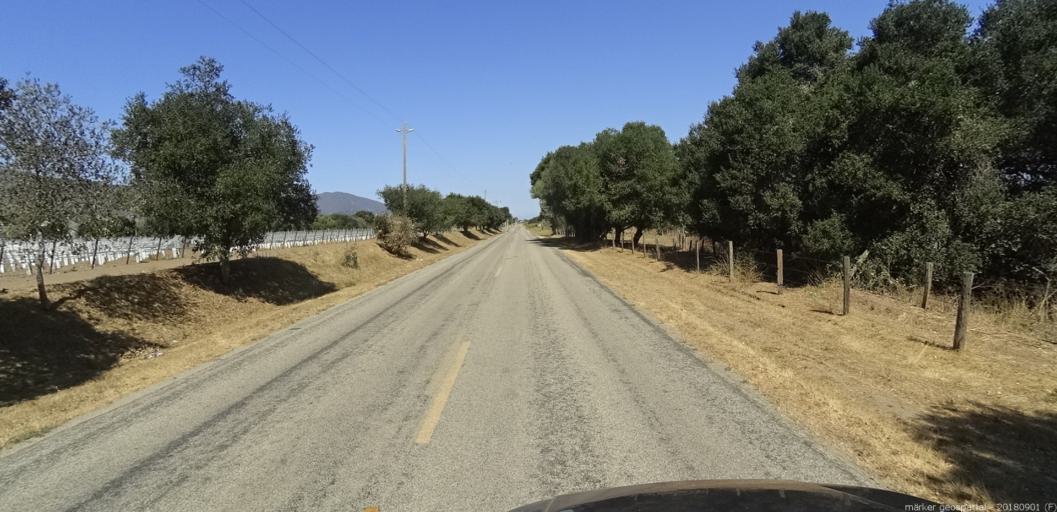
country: US
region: California
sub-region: Monterey County
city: Gonzales
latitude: 36.4963
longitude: -121.4992
